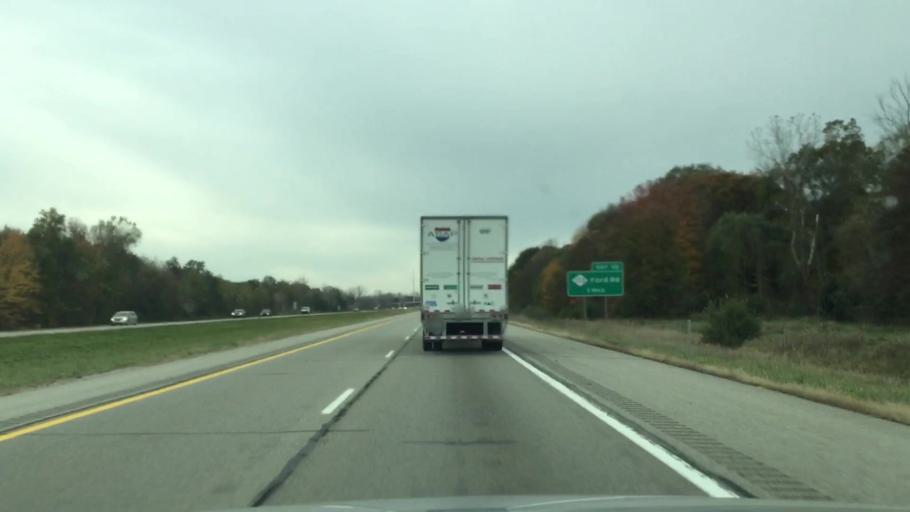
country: US
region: Michigan
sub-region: Washtenaw County
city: Ypsilanti
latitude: 42.3333
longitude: -83.6181
